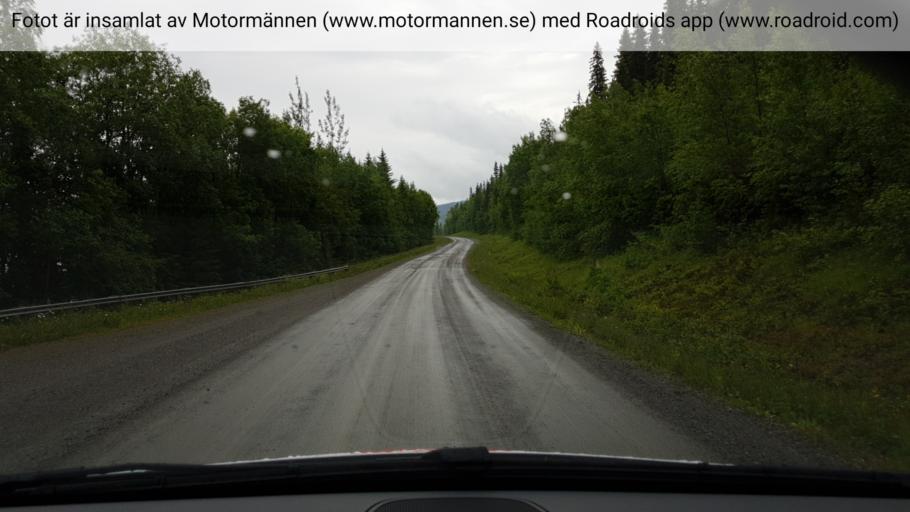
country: SE
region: Jaemtland
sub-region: Stroemsunds Kommun
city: Stroemsund
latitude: 64.2894
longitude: 15.0033
